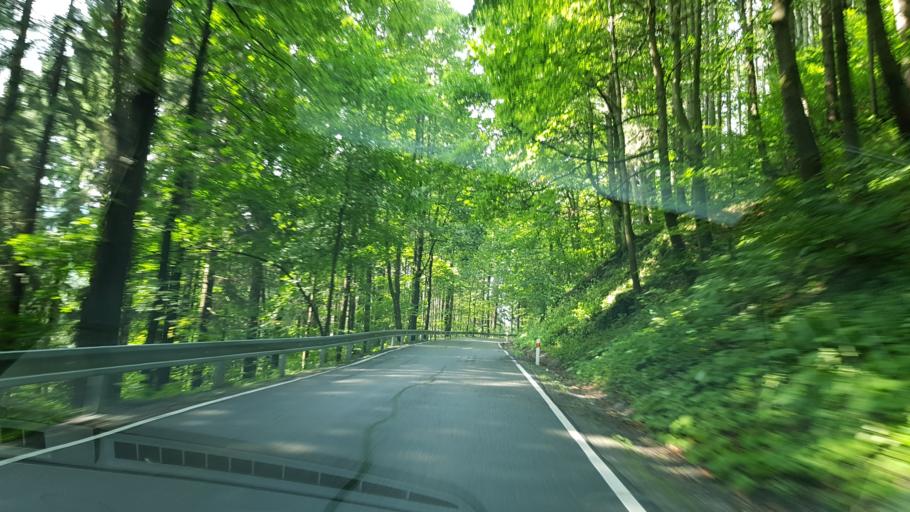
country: CZ
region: Olomoucky
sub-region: Okres Jesenik
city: Jesenik
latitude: 50.2082
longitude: 17.2446
